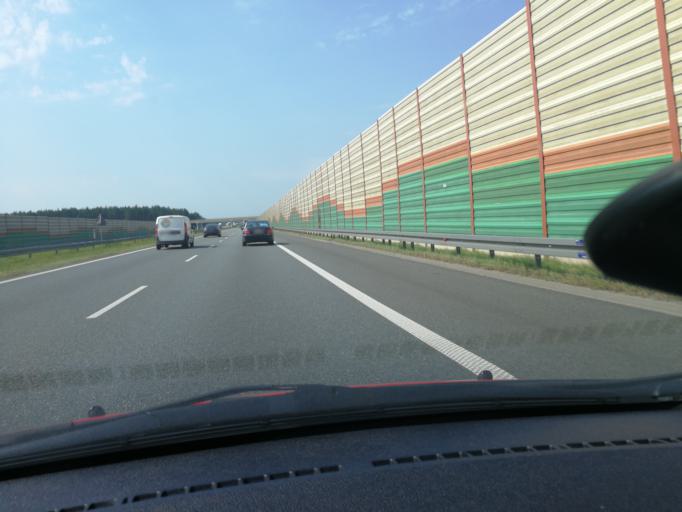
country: PL
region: Lodz Voivodeship
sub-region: Powiat skierniewicki
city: Bolimow
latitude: 52.0659
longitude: 20.1744
